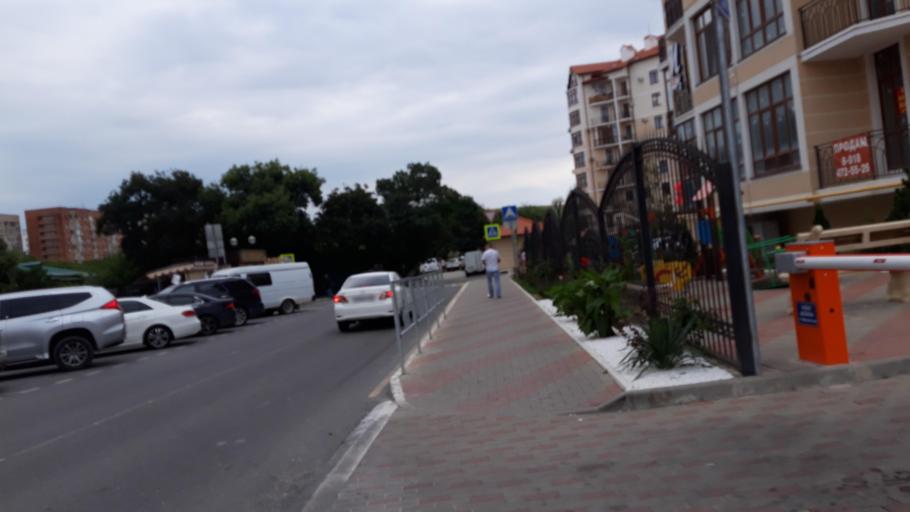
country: RU
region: Krasnodarskiy
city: Gelendzhik
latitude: 44.5507
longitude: 38.0606
